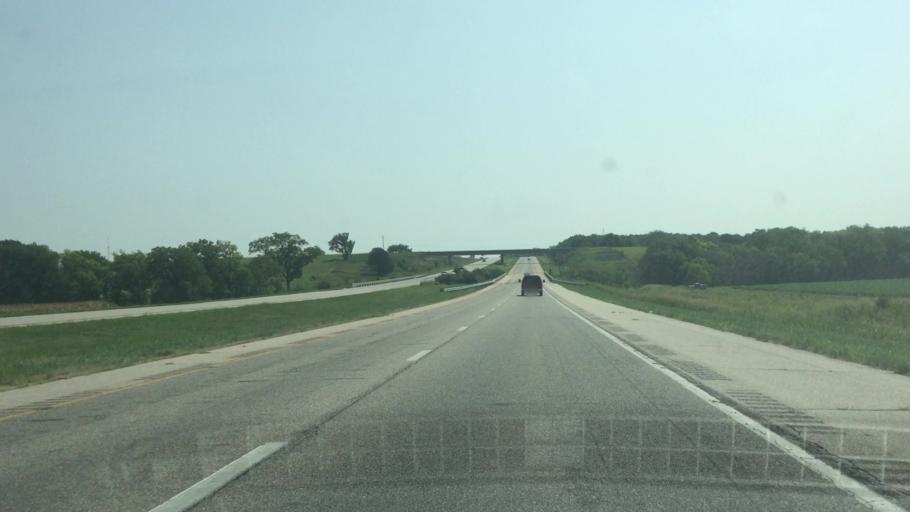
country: US
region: Kansas
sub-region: Osage County
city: Lyndon
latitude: 38.4262
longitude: -95.7531
